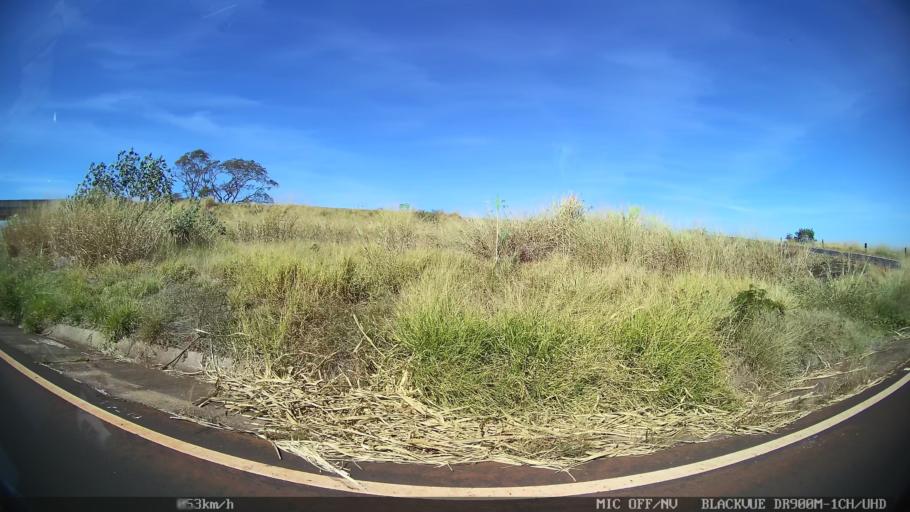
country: BR
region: Sao Paulo
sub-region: Nuporanga
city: Nuporanga
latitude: -20.5618
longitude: -47.6263
